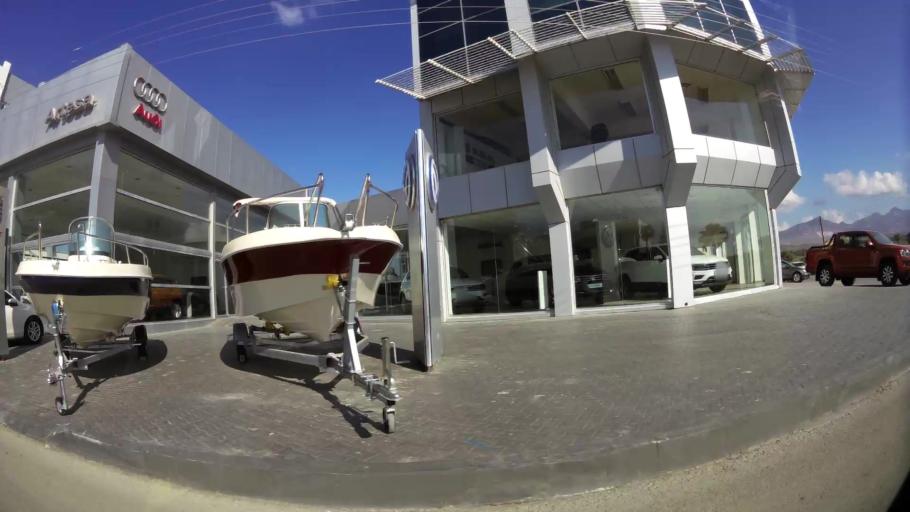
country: CY
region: Lefkosia
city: Nicosia
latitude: 35.2097
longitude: 33.3207
